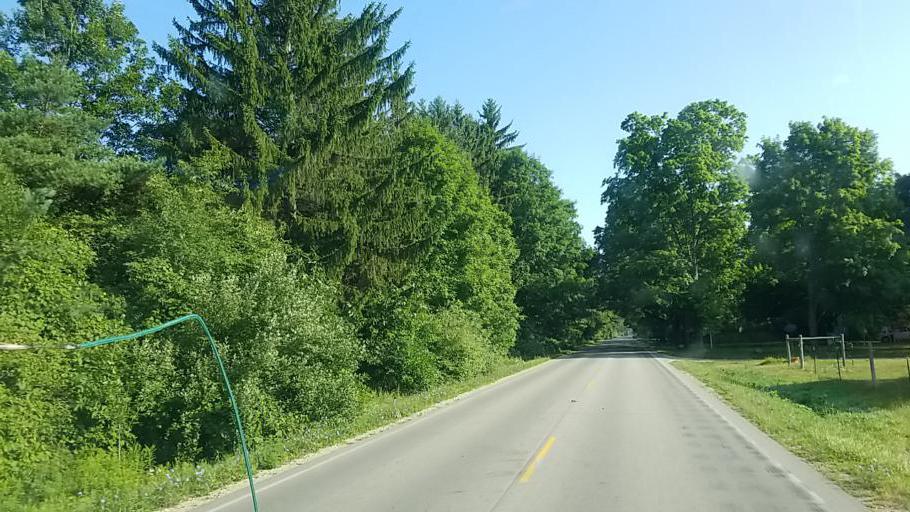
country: US
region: Michigan
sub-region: Newaygo County
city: Fremont
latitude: 43.3859
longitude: -85.9394
